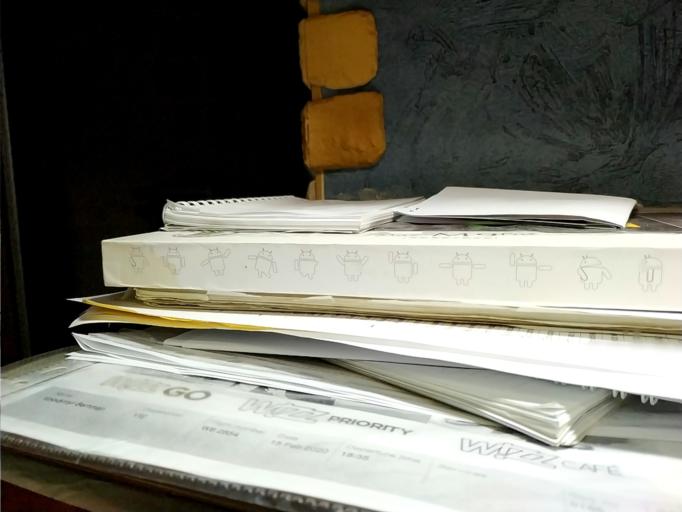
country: RU
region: Arkhangelskaya
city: Onega
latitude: 63.4601
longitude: 38.1692
